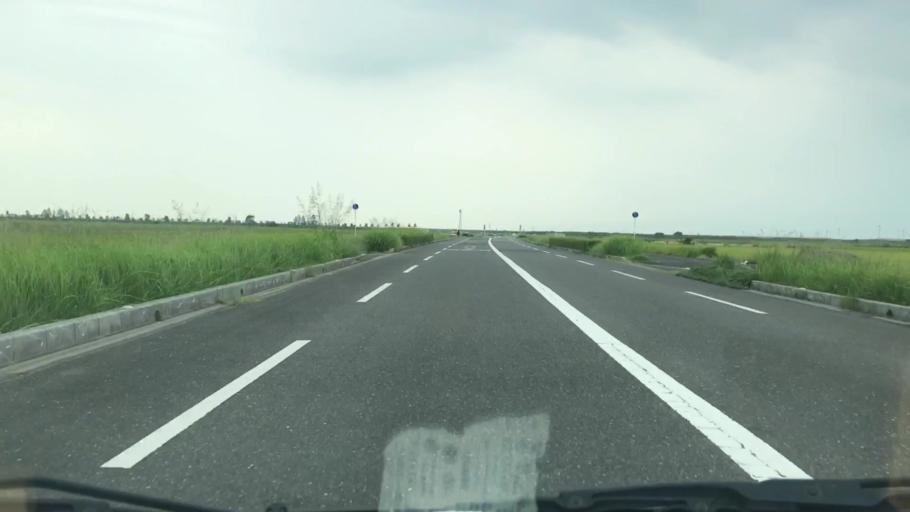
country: JP
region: Saga Prefecture
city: Okawa
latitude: 33.1677
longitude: 130.2933
